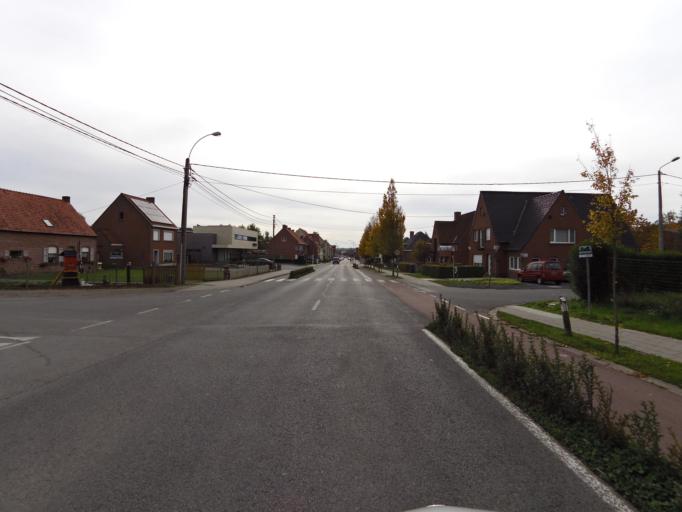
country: BE
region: Flanders
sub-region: Provincie West-Vlaanderen
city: Torhout
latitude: 51.0756
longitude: 3.0986
